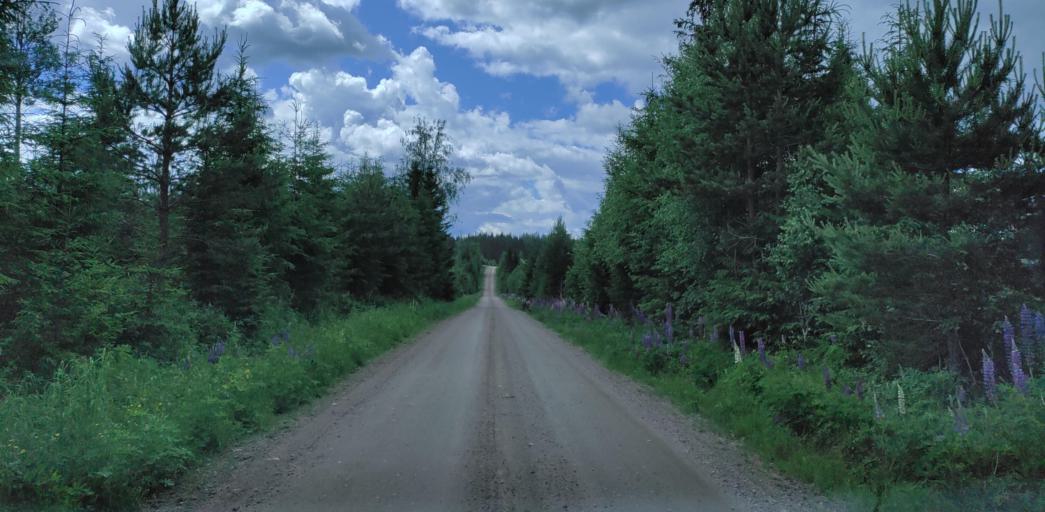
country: SE
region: Vaermland
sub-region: Hagfors Kommun
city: Ekshaerad
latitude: 60.0878
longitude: 13.3292
